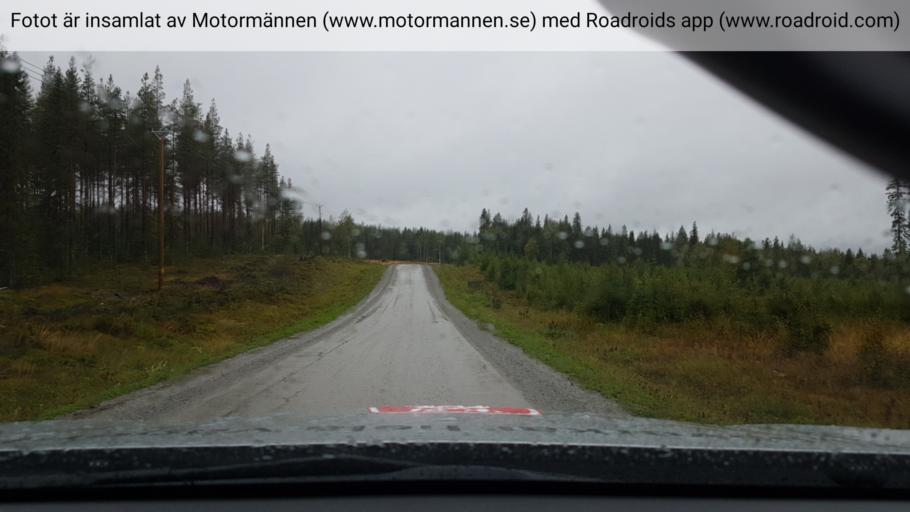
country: SE
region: Vaesterbotten
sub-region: Asele Kommun
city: Insjon
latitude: 64.0876
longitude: 17.7603
